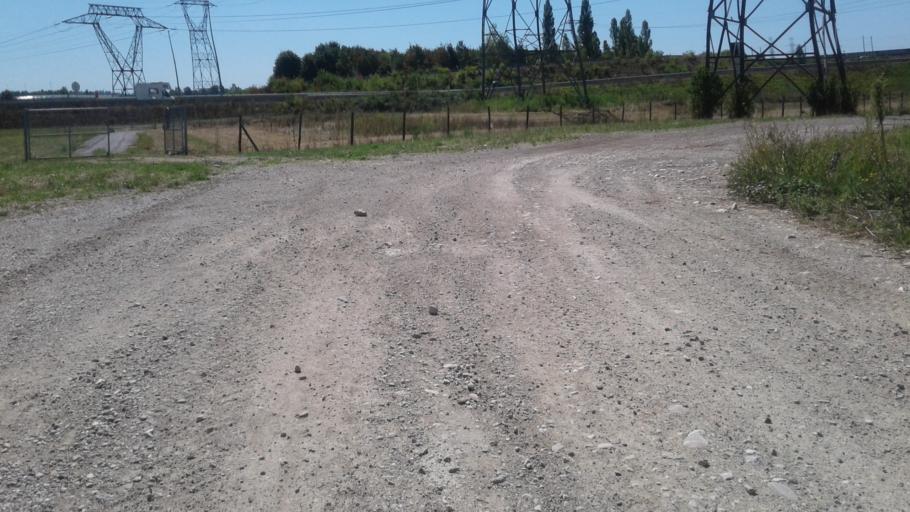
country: FR
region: Rhone-Alpes
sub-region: Departement de l'Ain
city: La Boisse
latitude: 45.8356
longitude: 5.0278
